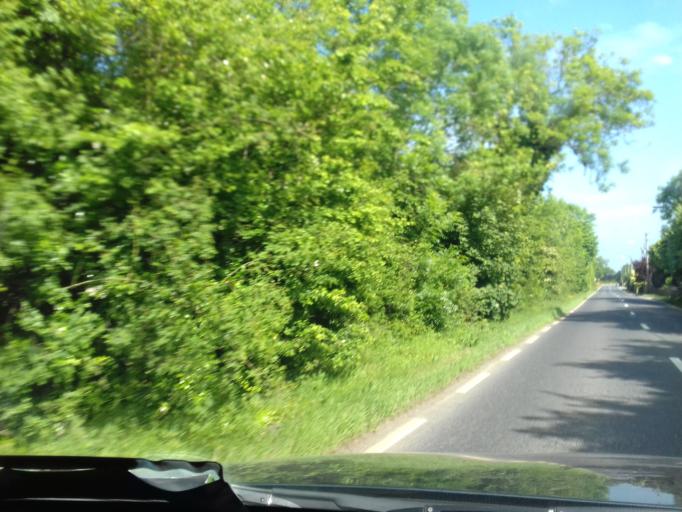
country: IE
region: Leinster
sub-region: Fingal County
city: Swords
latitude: 53.4730
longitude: -6.2558
